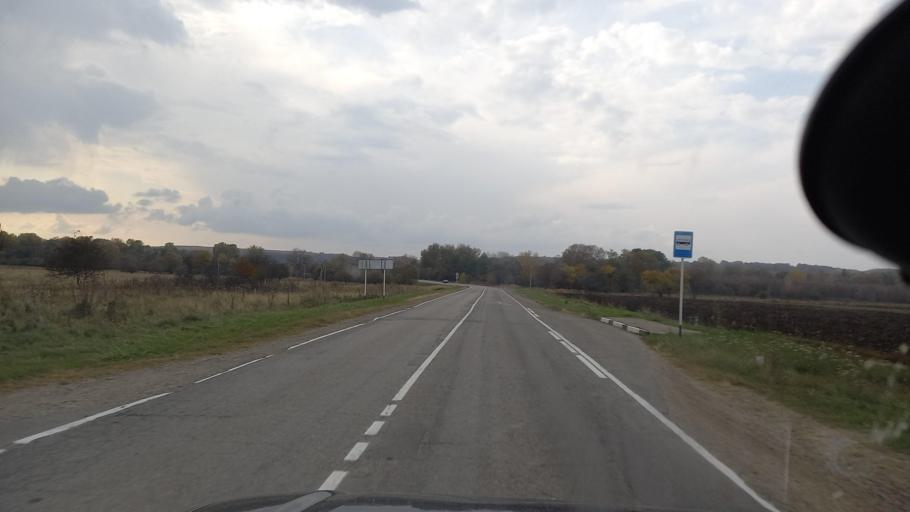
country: RU
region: Krasnodarskiy
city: Mostovskoy
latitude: 44.3922
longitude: 40.7538
